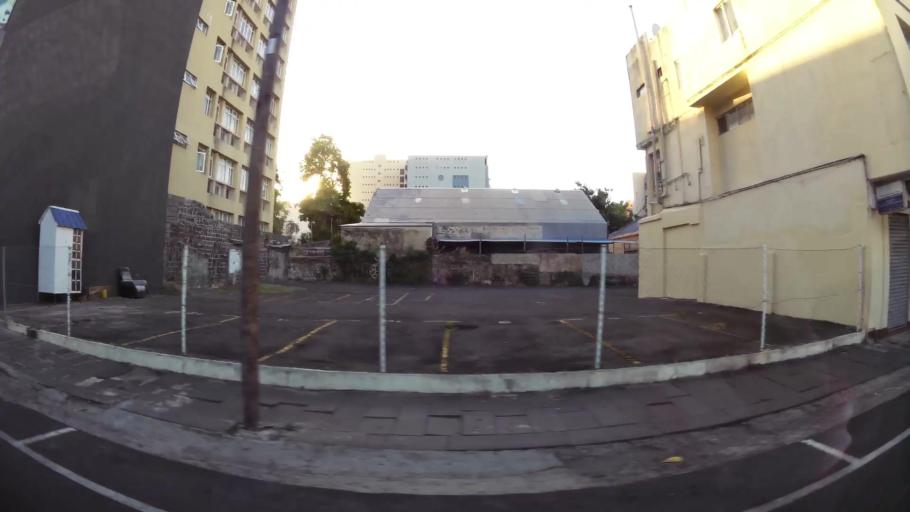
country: MU
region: Port Louis
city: Port Louis
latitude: -20.1658
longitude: 57.5011
